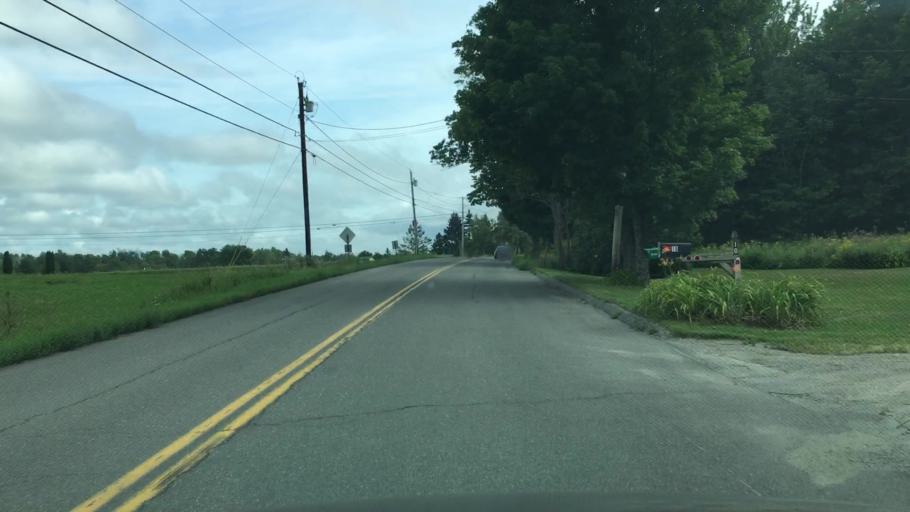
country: US
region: Maine
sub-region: Waldo County
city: Winterport
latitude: 44.6806
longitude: -68.8679
